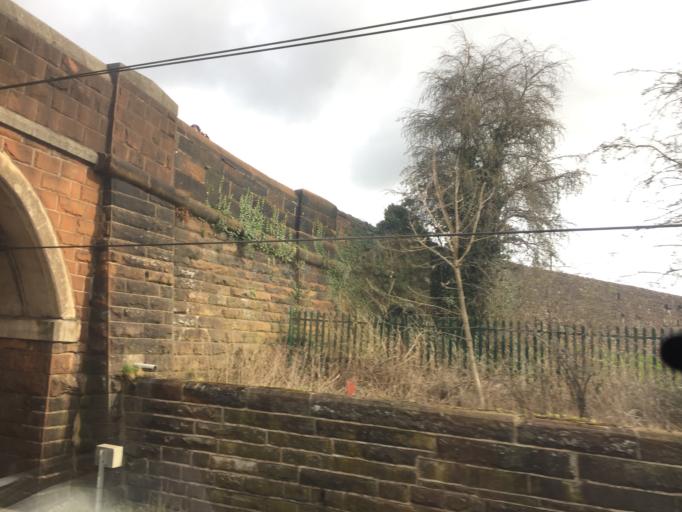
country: GB
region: England
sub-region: Cumbria
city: Penrith
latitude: 54.6634
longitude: -2.7585
